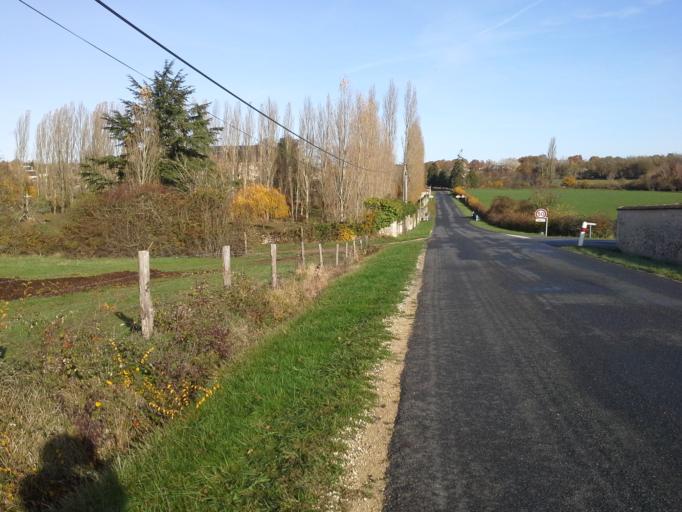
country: FR
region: Poitou-Charentes
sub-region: Departement de la Vienne
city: Pleumartin
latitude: 46.6381
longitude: 0.7541
